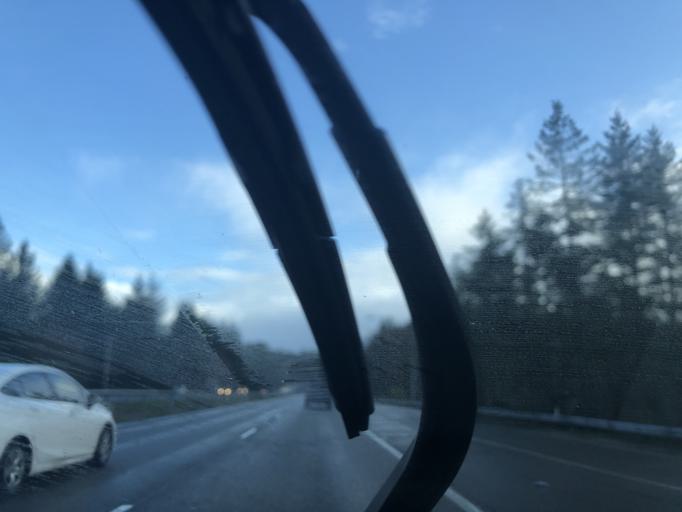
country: US
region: Washington
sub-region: Kitsap County
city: Erlands Point-Kitsap Lake
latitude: 47.6014
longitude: -122.7064
